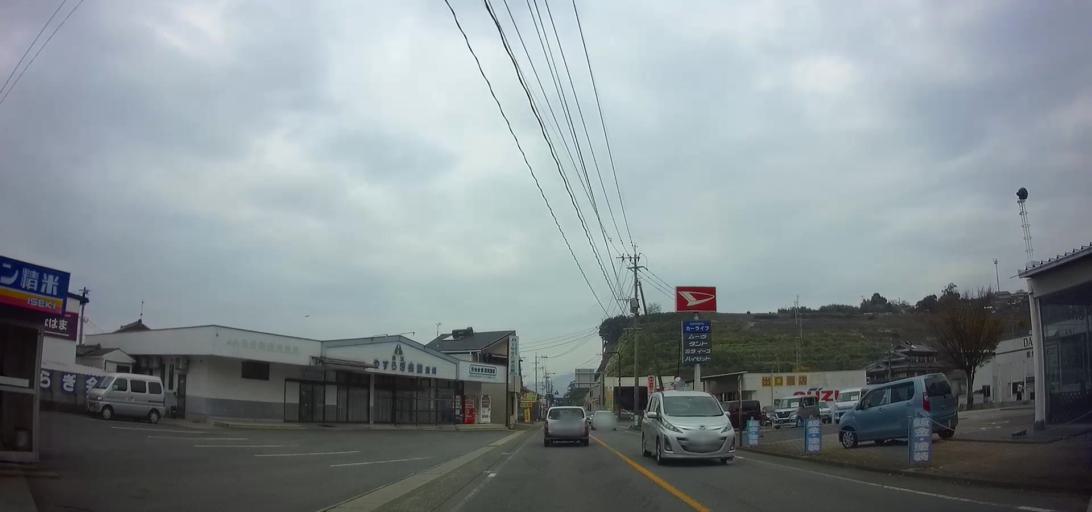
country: JP
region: Nagasaki
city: Shimabara
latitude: 32.7094
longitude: 130.1883
